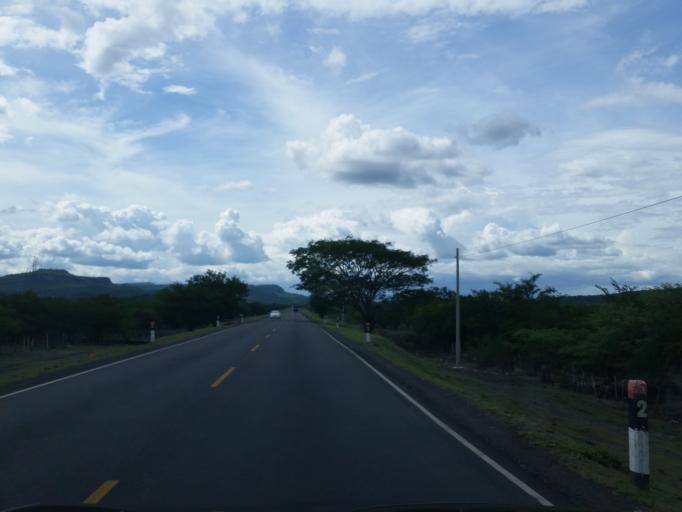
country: NI
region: Matagalpa
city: Ciudad Dario
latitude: 12.6449
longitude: -86.0677
